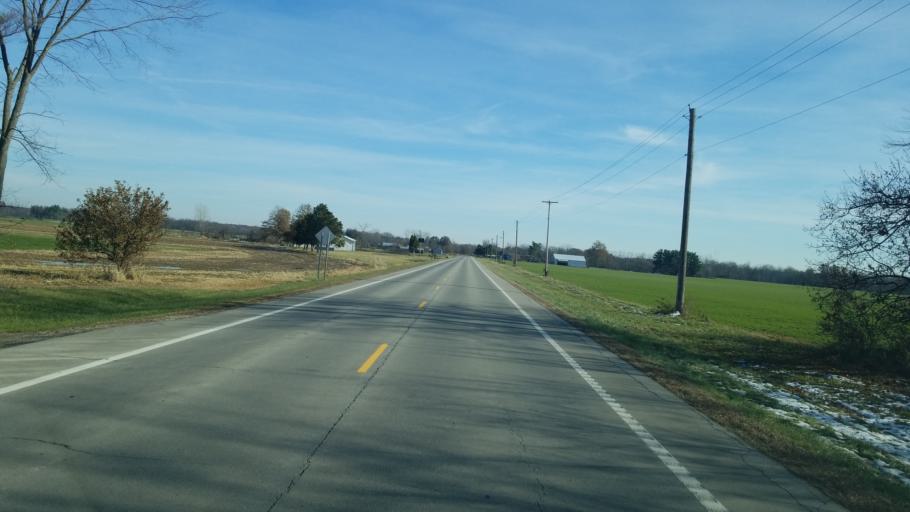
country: US
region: Ohio
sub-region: Huron County
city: Wakeman
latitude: 41.2031
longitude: -82.4246
